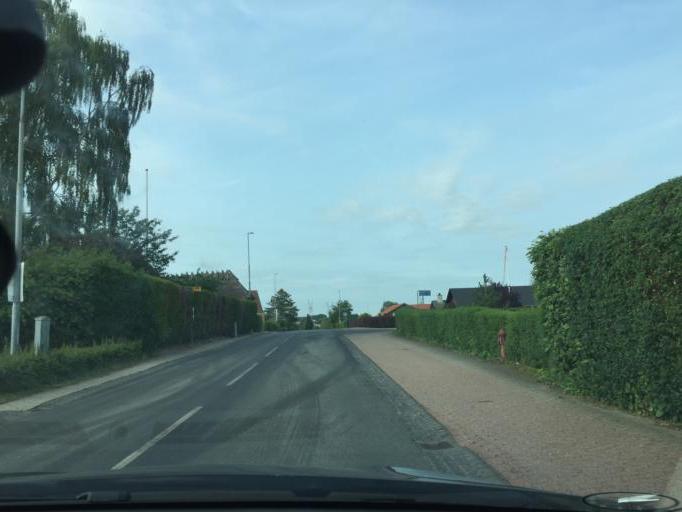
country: DK
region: South Denmark
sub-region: Odense Kommune
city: Bellinge
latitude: 55.3354
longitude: 10.3246
